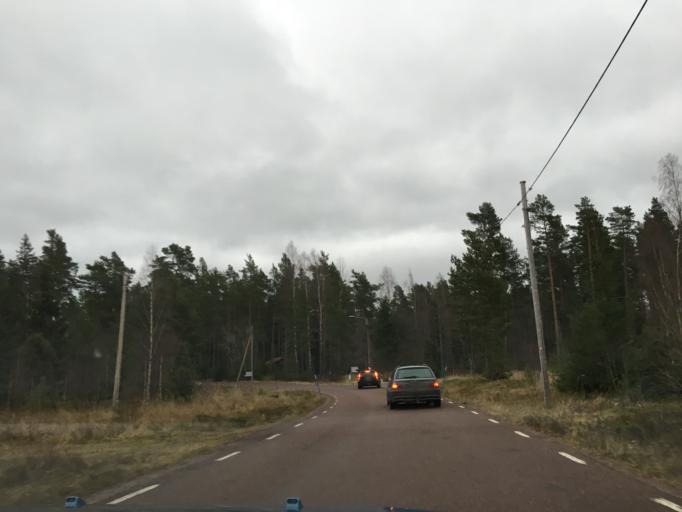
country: SE
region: Uppsala
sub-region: Alvkarleby Kommun
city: AElvkarleby
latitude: 60.6455
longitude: 17.5357
